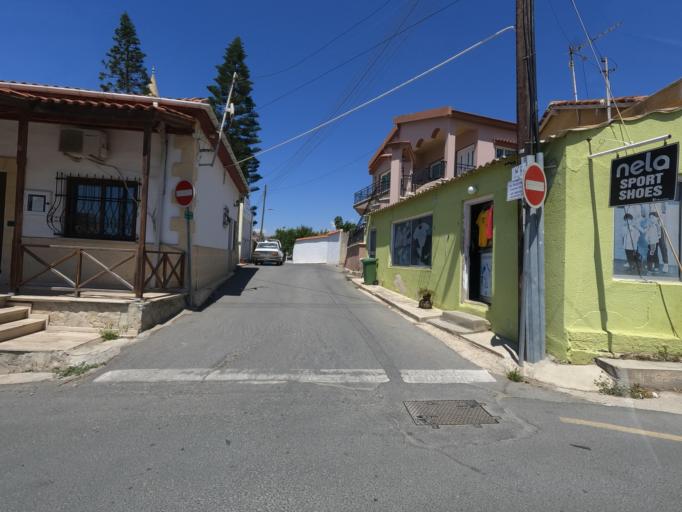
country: CY
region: Larnaka
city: Pyla
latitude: 35.0137
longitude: 33.6924
